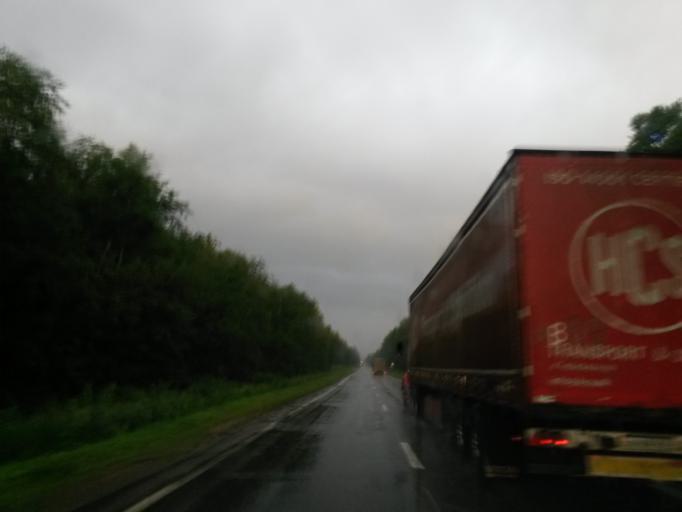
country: RU
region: Jaroslavl
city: Gavrilov-Yam
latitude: 57.4336
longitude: 39.9180
